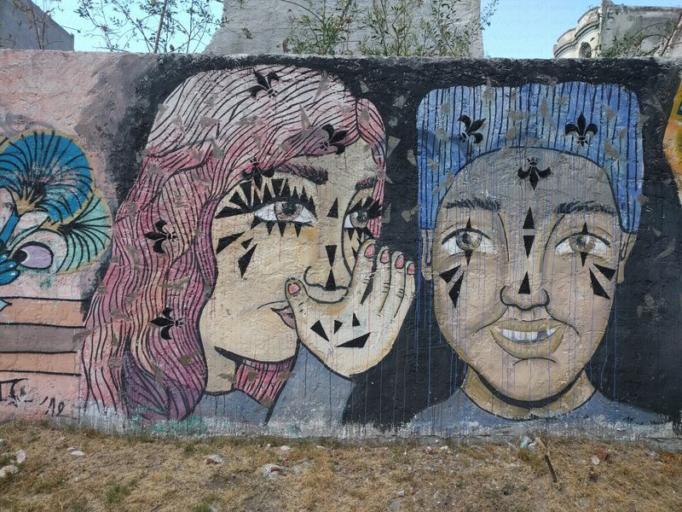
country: UY
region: Montevideo
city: Montevideo
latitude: -34.9063
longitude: -56.2087
